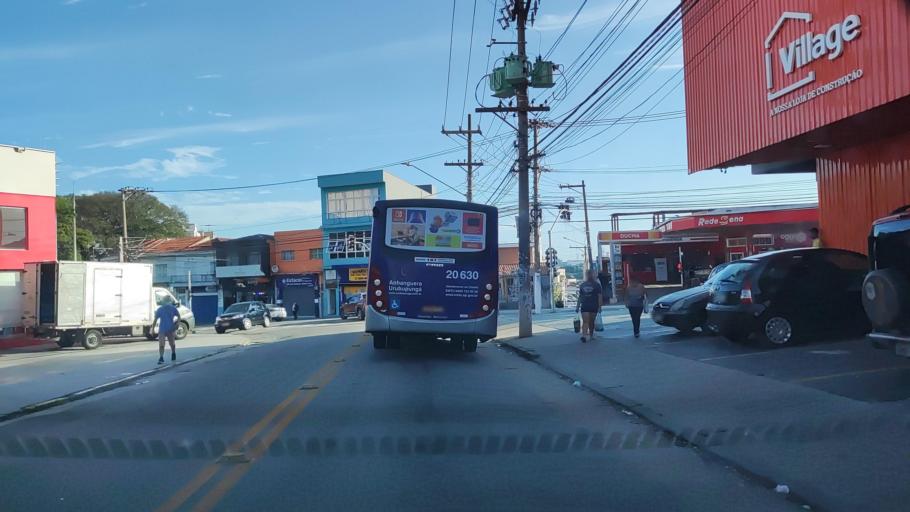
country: BR
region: Sao Paulo
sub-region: Osasco
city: Osasco
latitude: -23.5166
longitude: -46.7536
